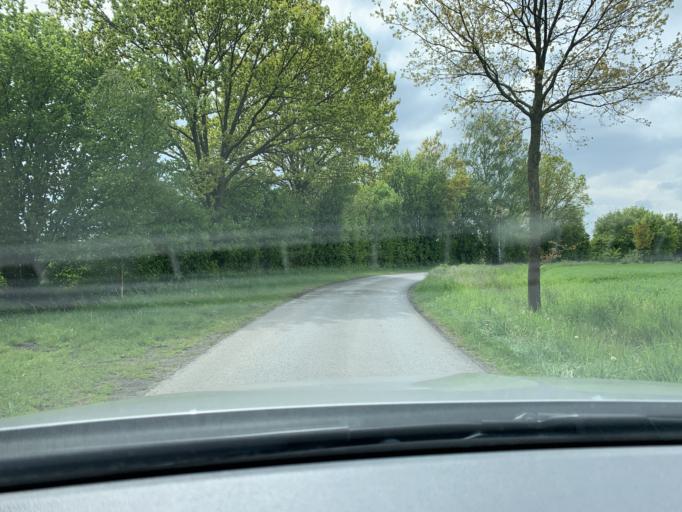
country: DE
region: North Rhine-Westphalia
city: Rietberg
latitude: 51.7939
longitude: 8.3834
